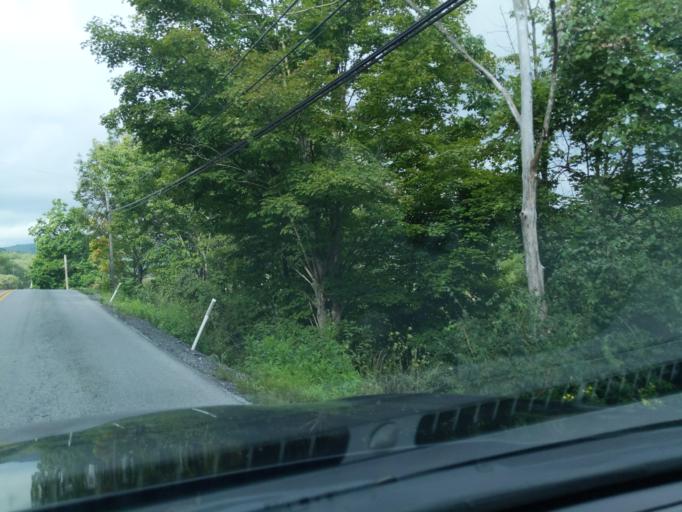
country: US
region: Pennsylvania
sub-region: Blair County
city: Roaring Spring
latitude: 40.3550
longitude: -78.4376
